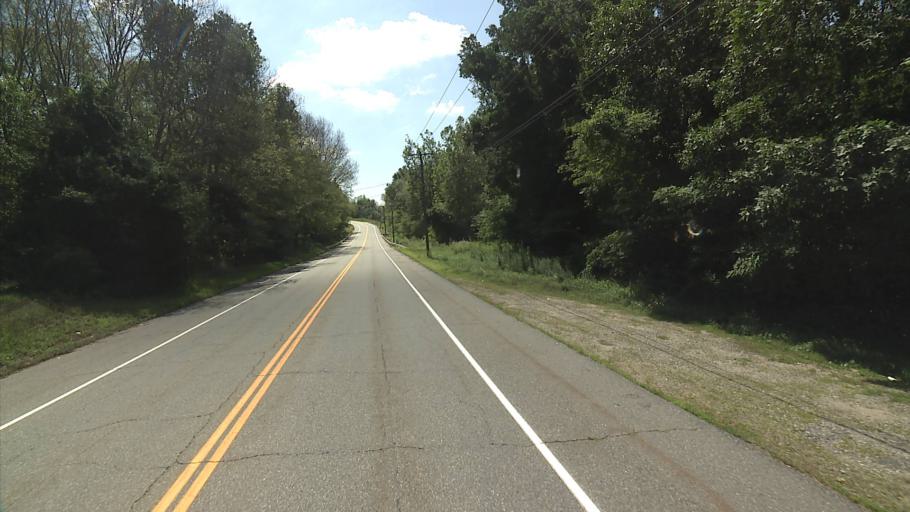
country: US
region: Connecticut
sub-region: Windham County
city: Plainfield Village
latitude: 41.6915
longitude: -71.9543
